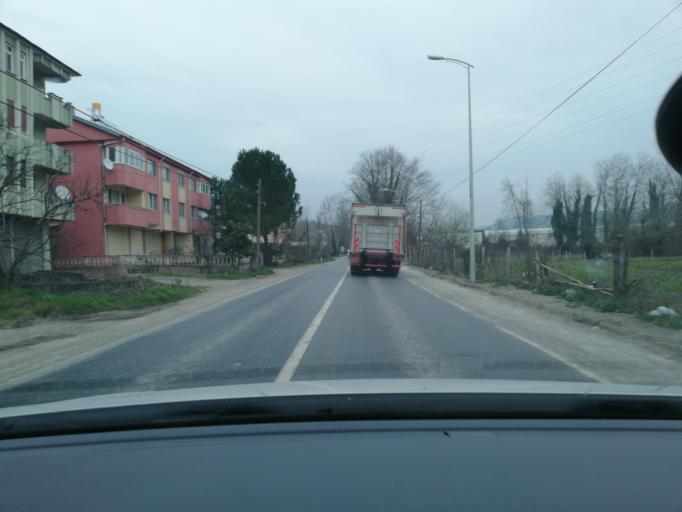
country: TR
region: Zonguldak
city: Gokcebey
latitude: 41.3008
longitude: 32.1209
